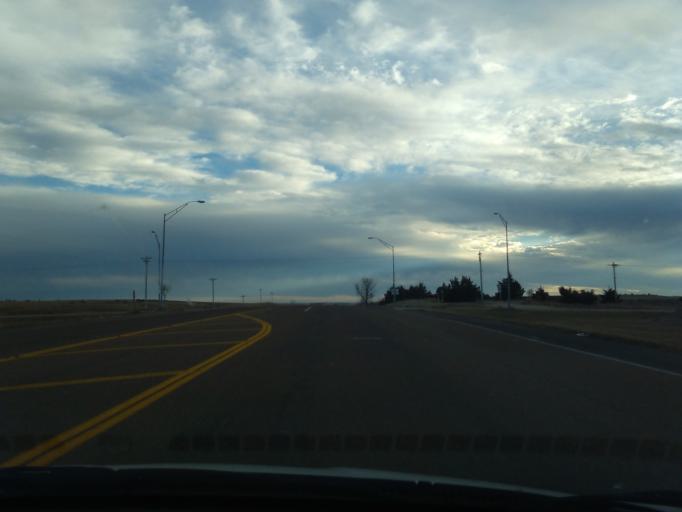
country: US
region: Nebraska
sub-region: Phelps County
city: Holdrege
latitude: 40.3079
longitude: -99.3684
